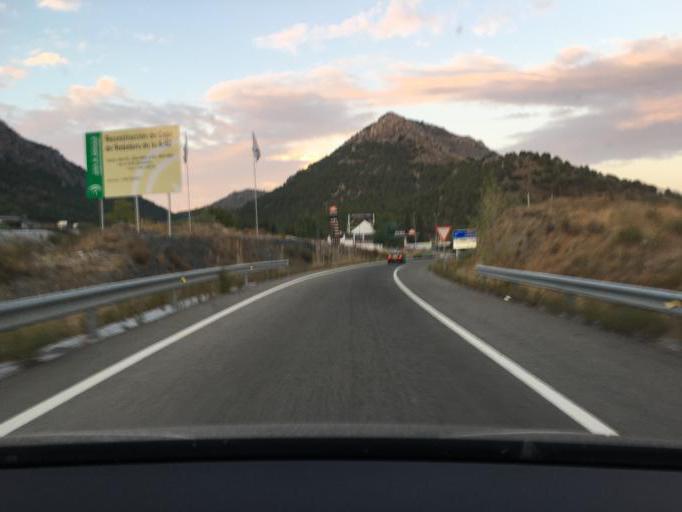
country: ES
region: Andalusia
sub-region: Provincia de Granada
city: Huetor Santillan
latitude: 37.2329
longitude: -3.4990
